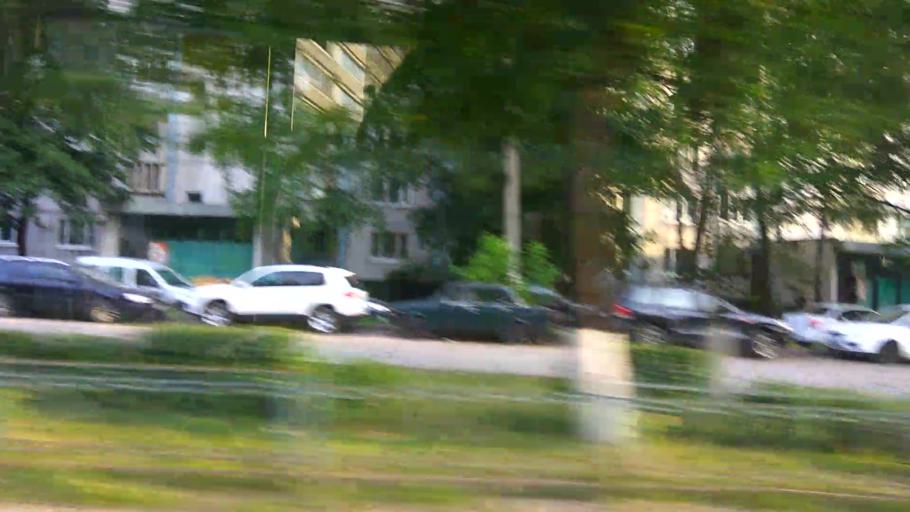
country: RU
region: Moskovskaya
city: Yubileyny
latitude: 55.9239
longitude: 37.8605
